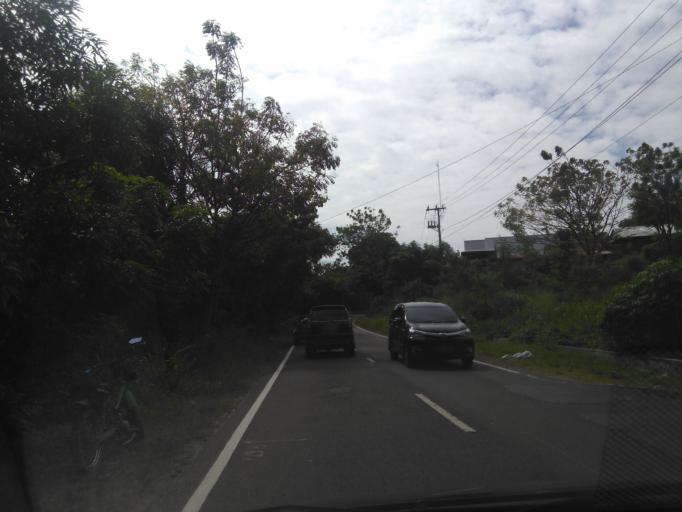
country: ID
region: South Sulawesi
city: Majennang
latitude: -3.9374
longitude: 119.6166
